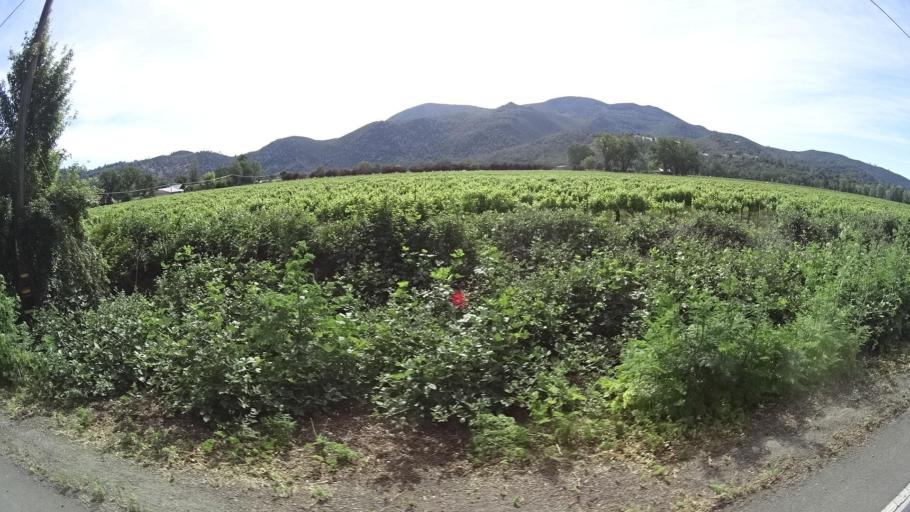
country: US
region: California
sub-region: Lake County
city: Kelseyville
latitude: 38.9881
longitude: -122.8291
